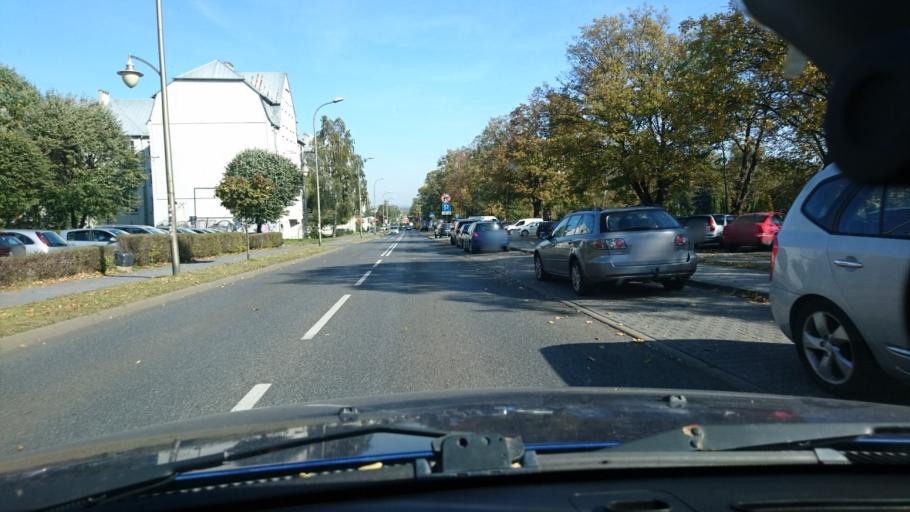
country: PL
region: Silesian Voivodeship
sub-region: Myslowice
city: Myslowice
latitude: 50.2372
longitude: 19.1305
